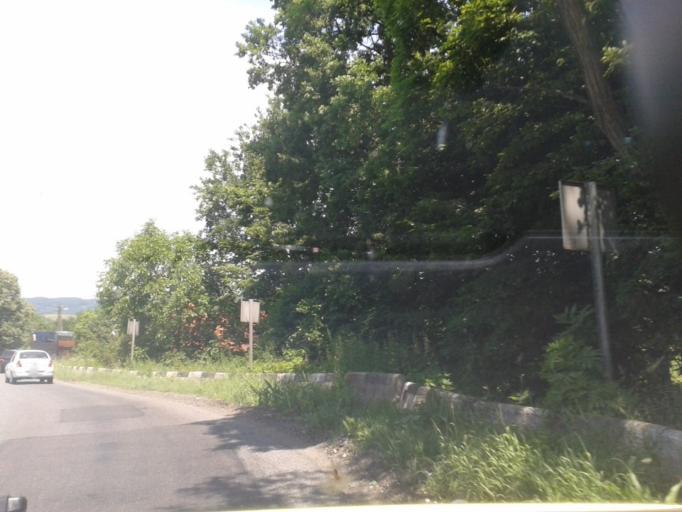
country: RO
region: Hunedoara
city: Lapugiu de Jos
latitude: 45.8852
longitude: 22.4429
